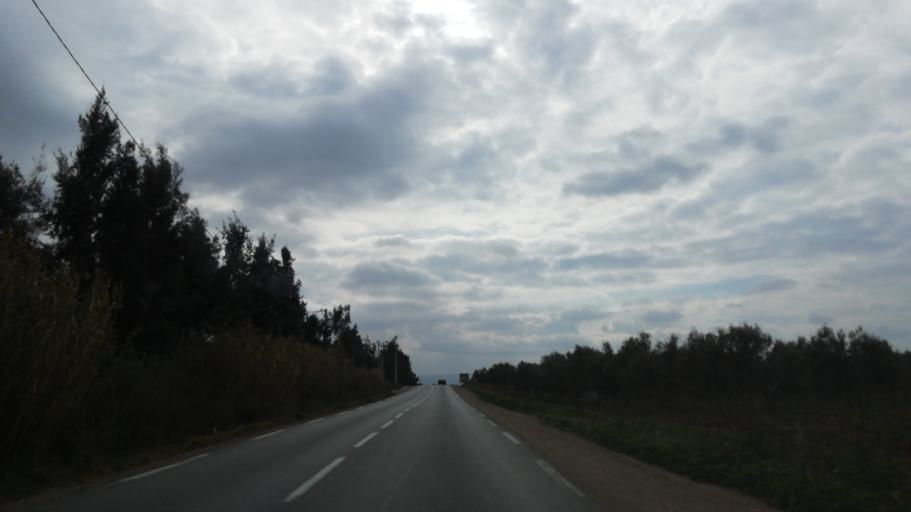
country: DZ
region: Oran
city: Sidi ech Chahmi
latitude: 35.5727
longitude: -0.4509
